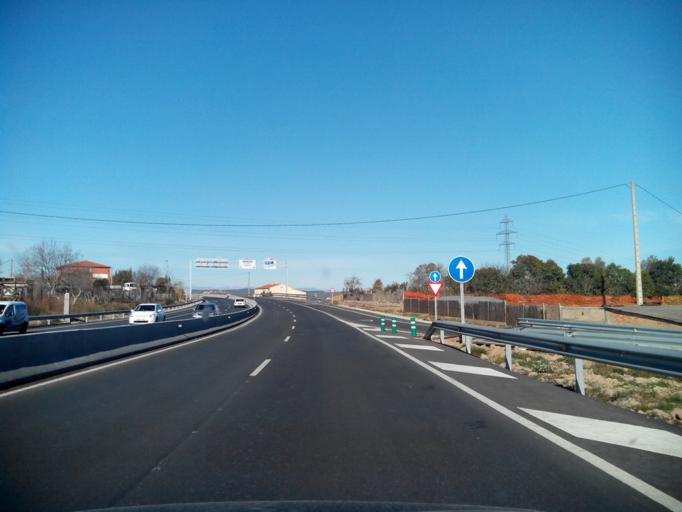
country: ES
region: Catalonia
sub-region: Provincia de Barcelona
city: Sant Fruitos de Bages
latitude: 41.7269
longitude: 1.8542
